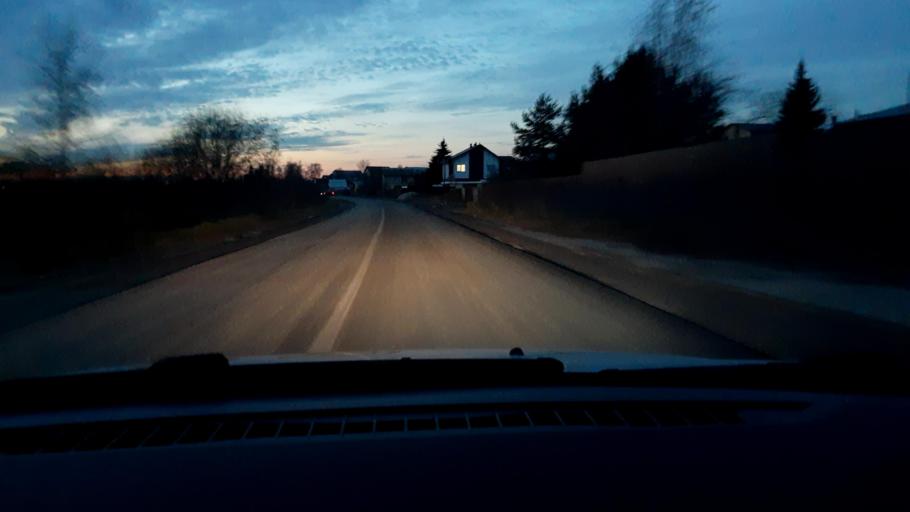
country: RU
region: Nizjnij Novgorod
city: Neklyudovo
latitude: 56.4168
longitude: 43.9700
